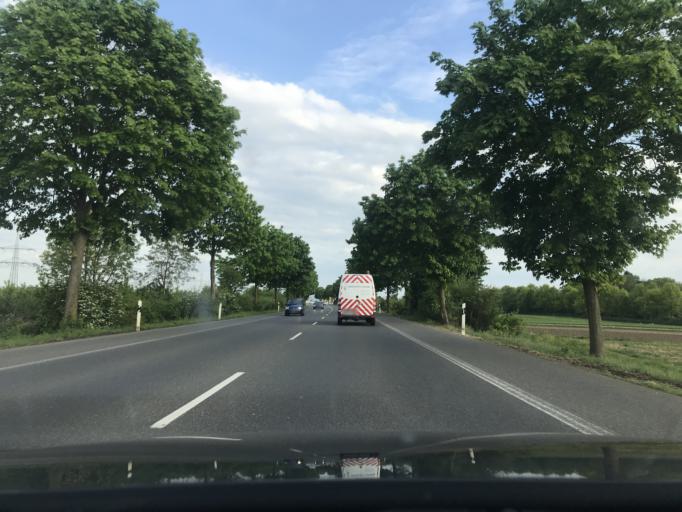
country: DE
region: North Rhine-Westphalia
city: Bornheim
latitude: 50.7715
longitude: 7.0009
